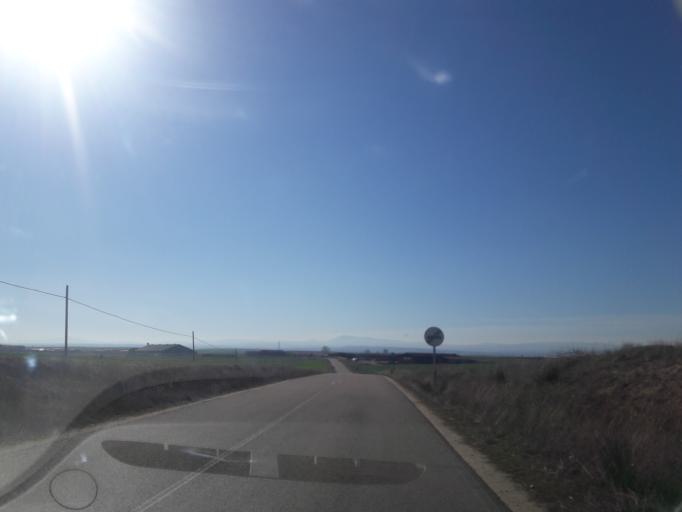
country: ES
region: Castille and Leon
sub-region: Provincia de Salamanca
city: Macotera
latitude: 40.8398
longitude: -5.3063
